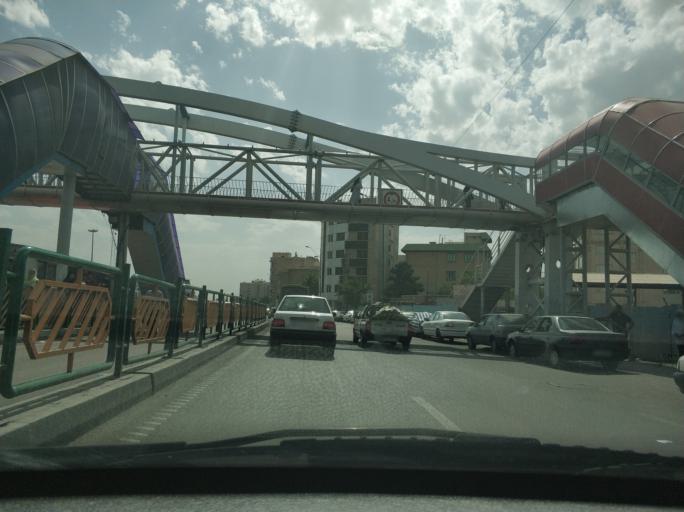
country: IR
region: Tehran
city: Tehran
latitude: 35.7236
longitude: 51.5194
